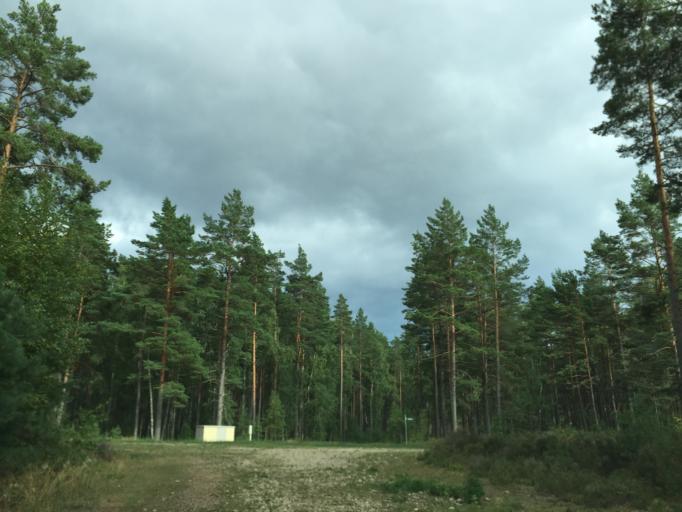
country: LV
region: Saulkrastu
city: Saulkrasti
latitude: 57.1768
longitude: 24.3721
